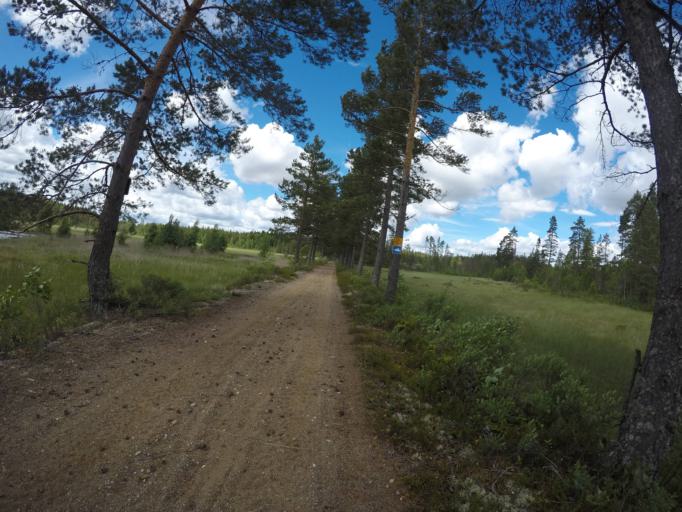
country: SE
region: Vaermland
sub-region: Filipstads Kommun
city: Lesjofors
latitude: 60.1381
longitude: 14.2981
